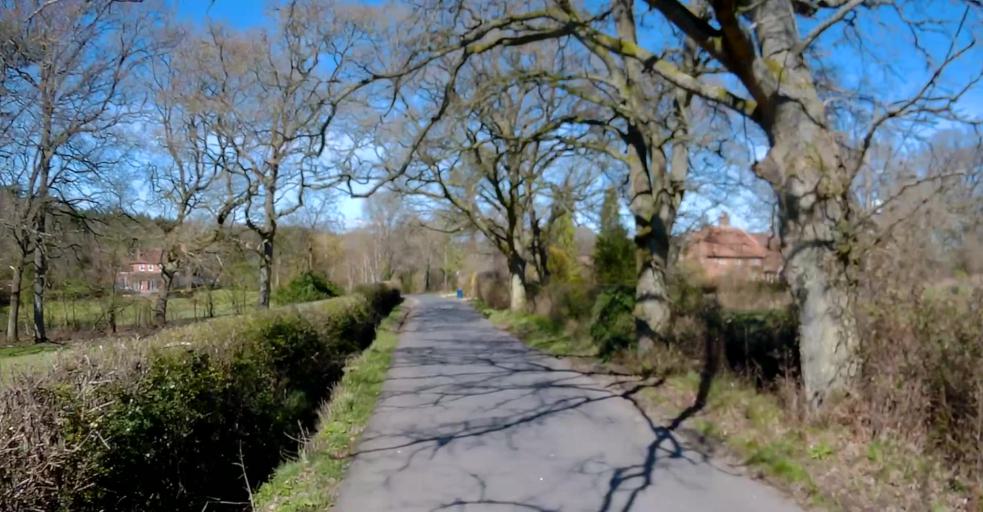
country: GB
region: England
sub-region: Hampshire
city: Lindford
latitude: 51.1664
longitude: -0.8284
